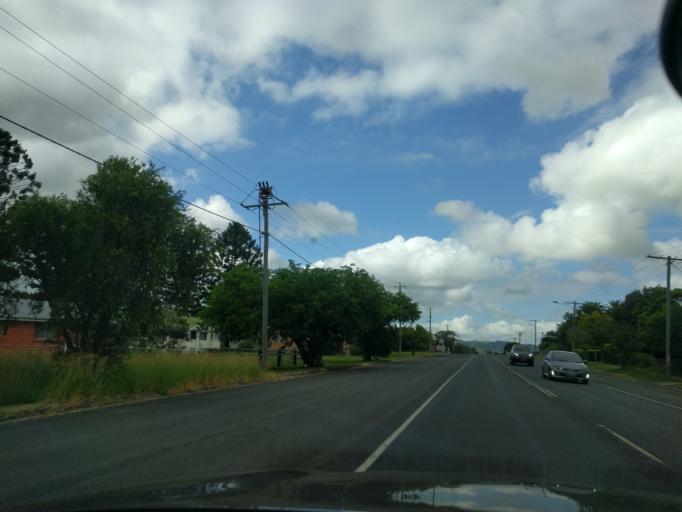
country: AU
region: Queensland
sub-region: Logan
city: Cedar Vale
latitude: -27.9934
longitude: 152.9914
